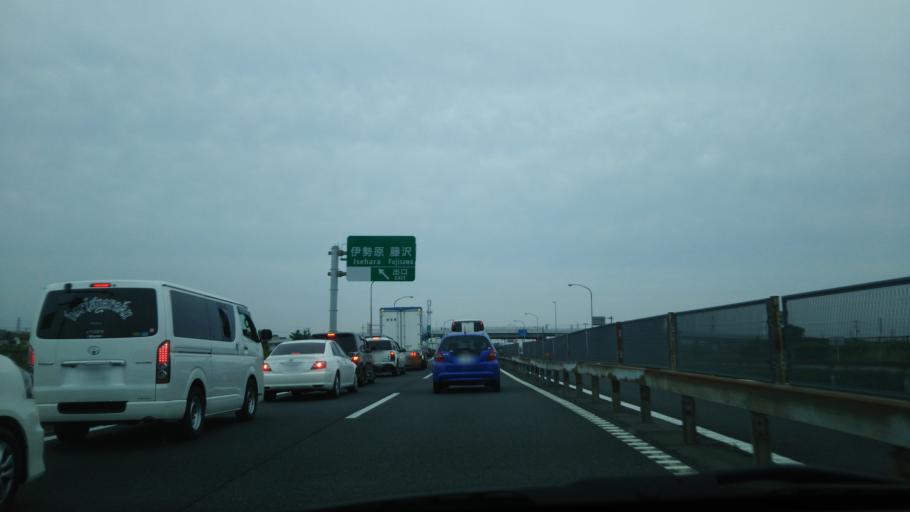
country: JP
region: Kanagawa
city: Isehara
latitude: 35.3836
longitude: 139.3304
